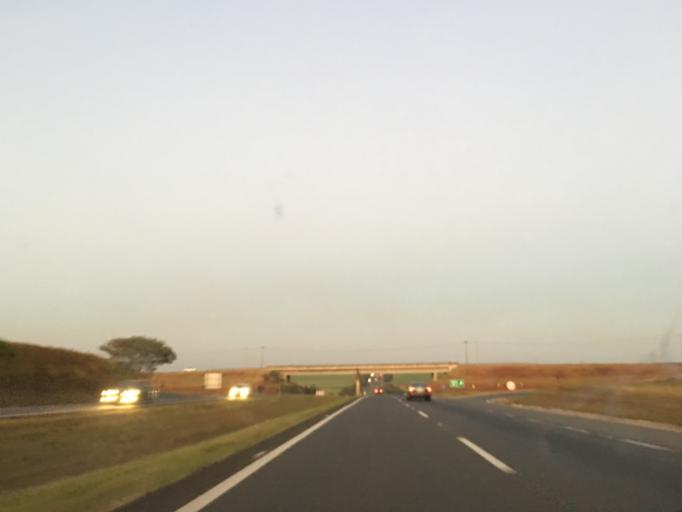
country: BR
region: Sao Paulo
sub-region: Piracicaba
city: Piracicaba
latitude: -22.7237
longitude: -47.5869
